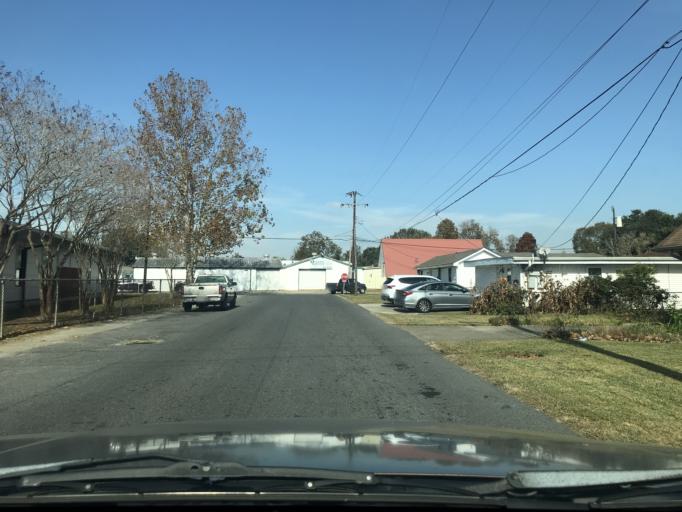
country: US
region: Louisiana
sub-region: Jefferson Parish
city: Marrero
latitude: 29.8995
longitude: -90.0905
